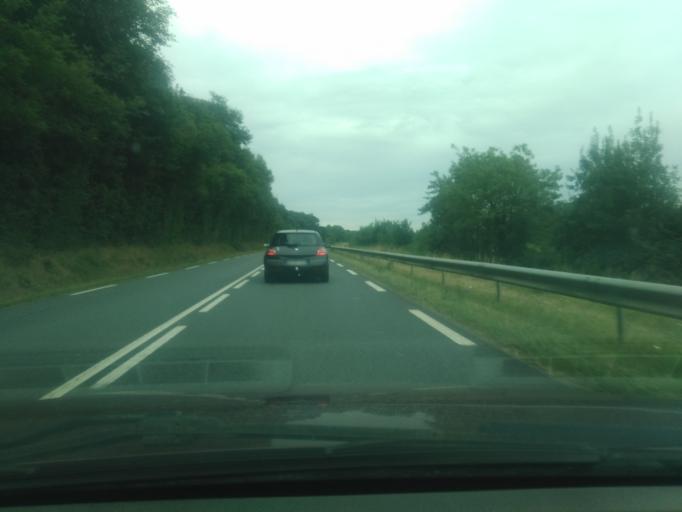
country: FR
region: Centre
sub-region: Departement de l'Indre
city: Le Blanc
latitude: 46.6339
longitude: 1.1132
